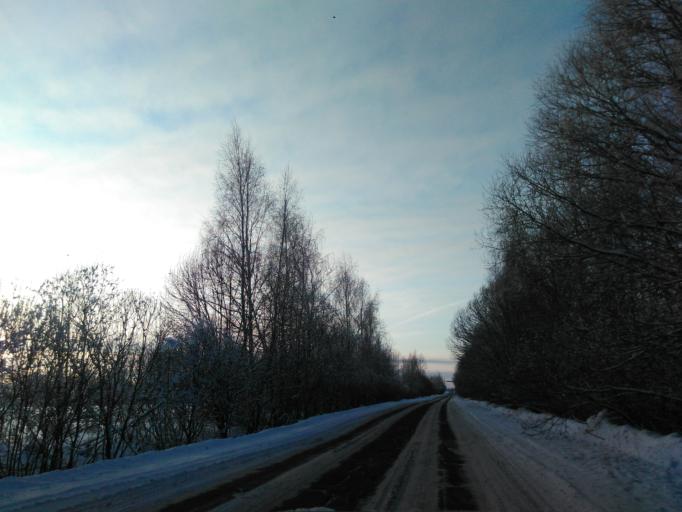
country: RU
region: Tverskaya
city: Zavidovo
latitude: 56.6280
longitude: 36.6158
